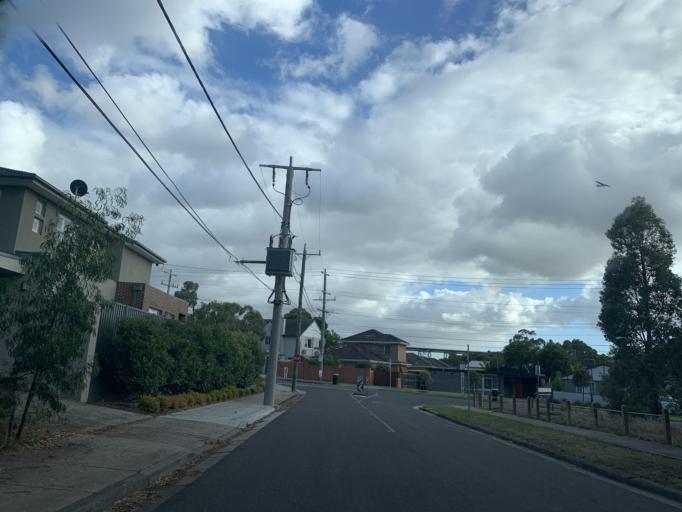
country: AU
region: Victoria
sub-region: Moreland
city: Gowanbrae
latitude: -37.7141
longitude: 144.8980
